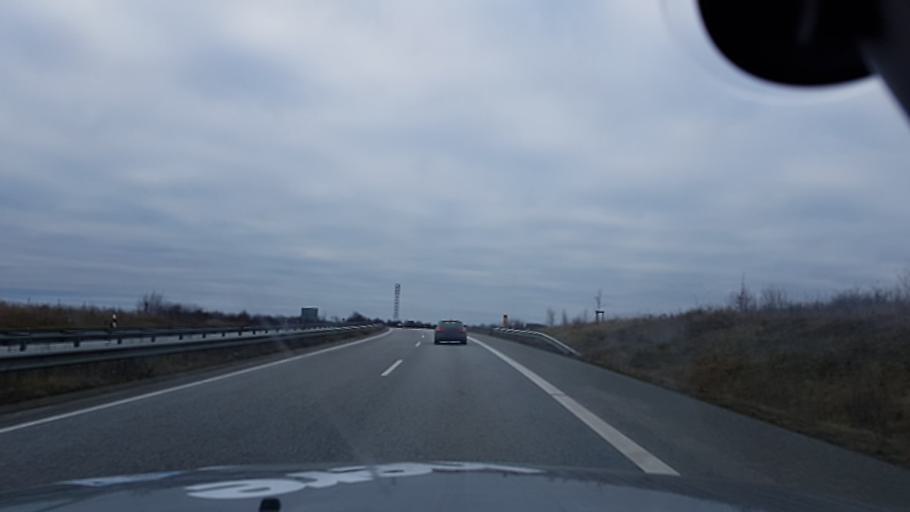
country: DE
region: Schleswig-Holstein
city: Gremersdorf
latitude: 54.3299
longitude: 10.9323
